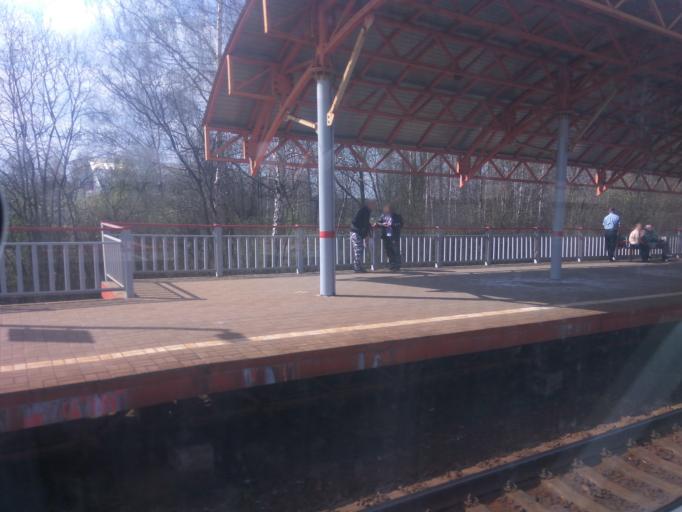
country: RU
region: Moskovskaya
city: Podosinki
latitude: 56.2076
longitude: 37.5262
